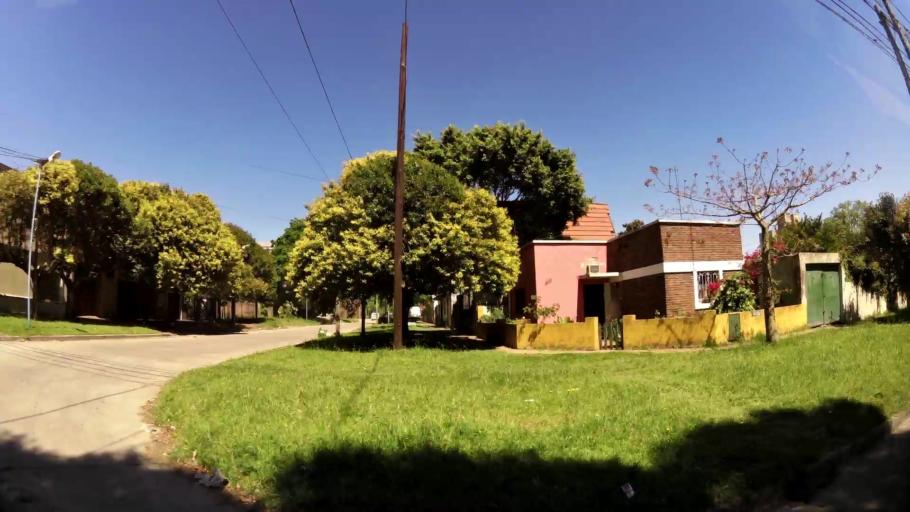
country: AR
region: Buenos Aires
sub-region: Partido de Quilmes
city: Quilmes
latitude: -34.7282
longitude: -58.2865
